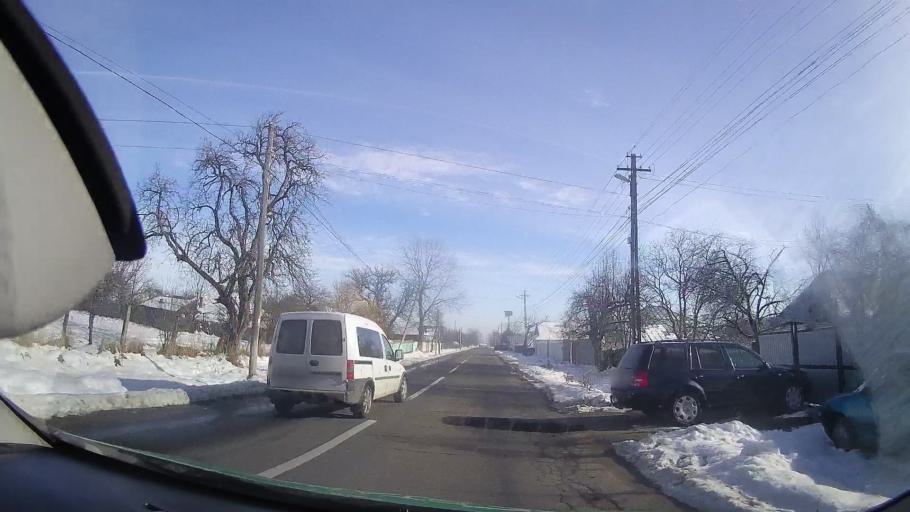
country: RO
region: Neamt
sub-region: Comuna Agapia
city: Agapia
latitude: 47.1741
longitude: 26.3027
